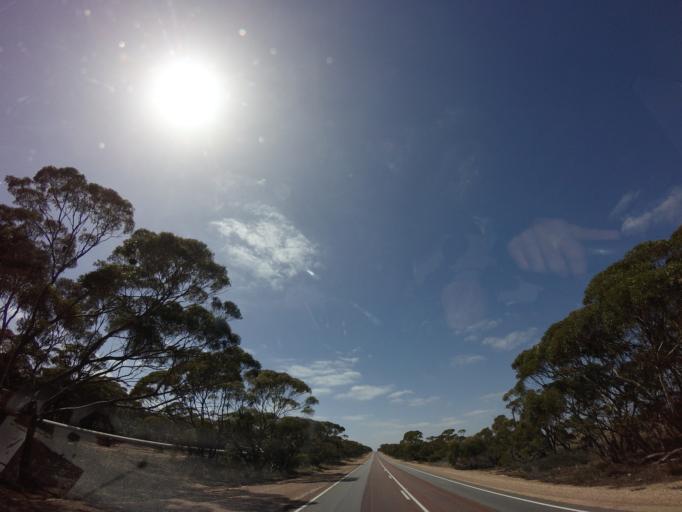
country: AU
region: South Australia
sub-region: Kimba
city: Caralue
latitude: -33.0921
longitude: 135.5136
